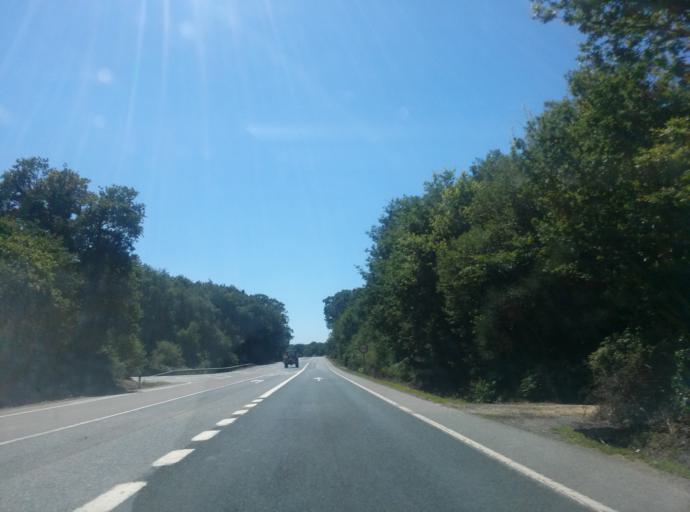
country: ES
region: Galicia
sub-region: Provincia de Lugo
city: Castro de Rei
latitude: 43.1157
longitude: -7.4447
